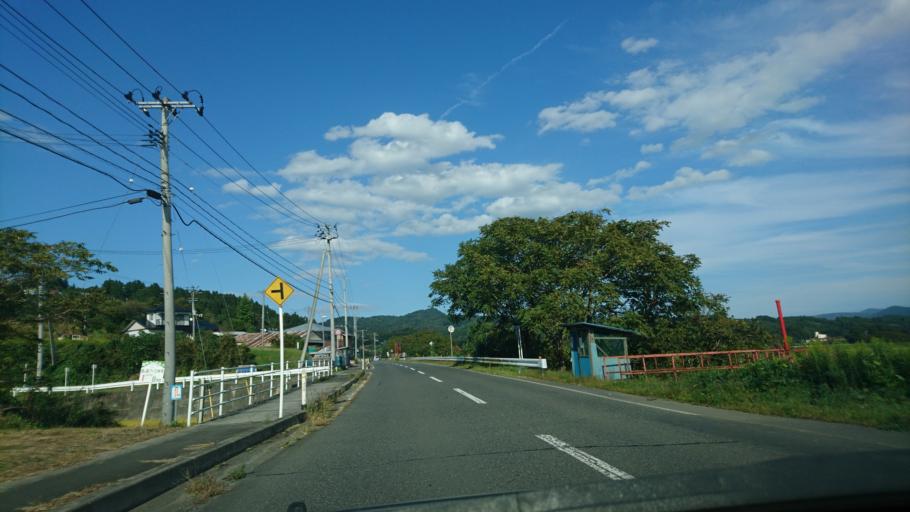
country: JP
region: Iwate
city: Ichinoseki
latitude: 38.8504
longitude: 141.2763
